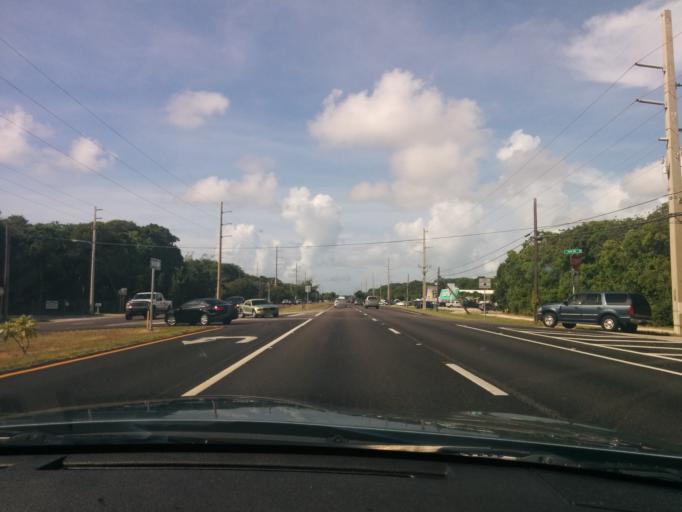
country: US
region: Florida
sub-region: Monroe County
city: Key Largo
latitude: 25.1103
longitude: -80.4255
